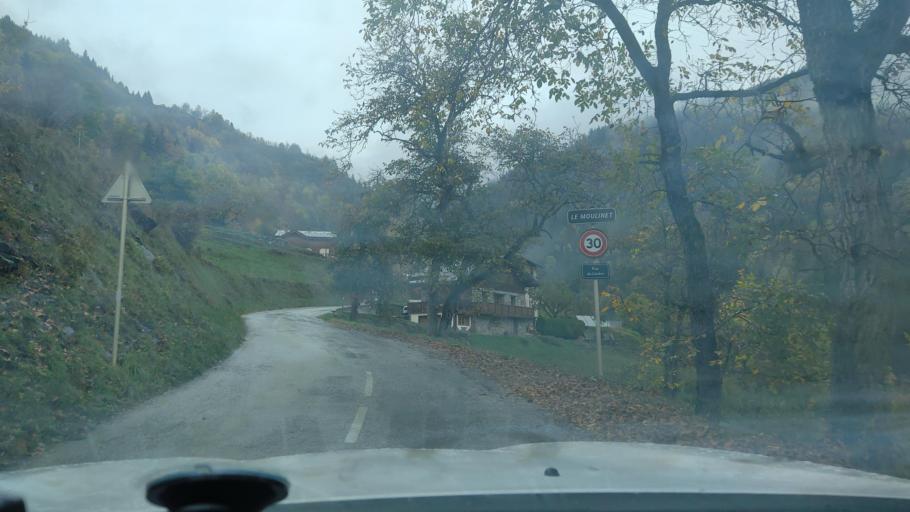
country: FR
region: Rhone-Alpes
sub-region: Departement de la Savoie
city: Bozel
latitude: 45.4500
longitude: 6.6462
